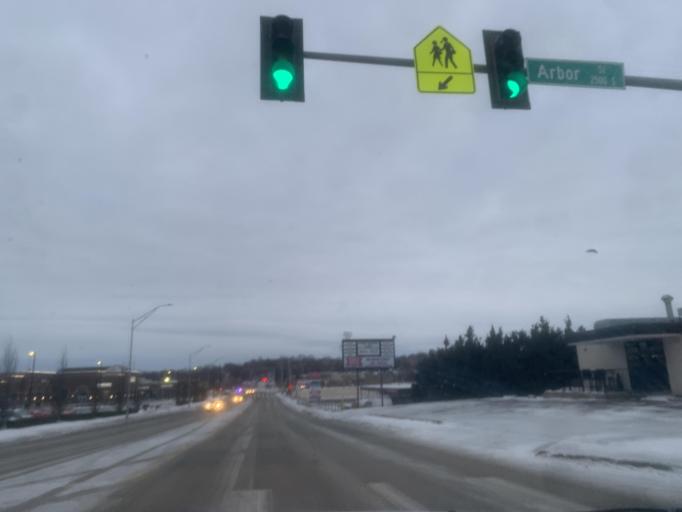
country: US
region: Nebraska
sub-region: Douglas County
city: Ralston
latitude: 41.2367
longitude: -96.0527
